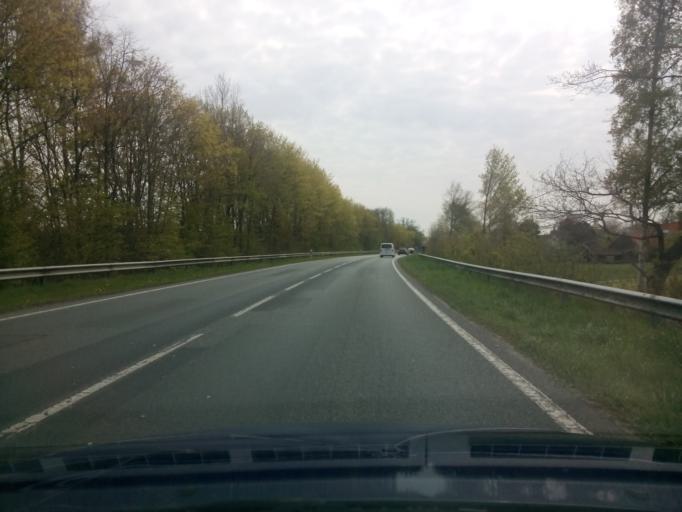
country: DE
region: Lower Saxony
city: Syke
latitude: 52.9428
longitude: 8.8264
